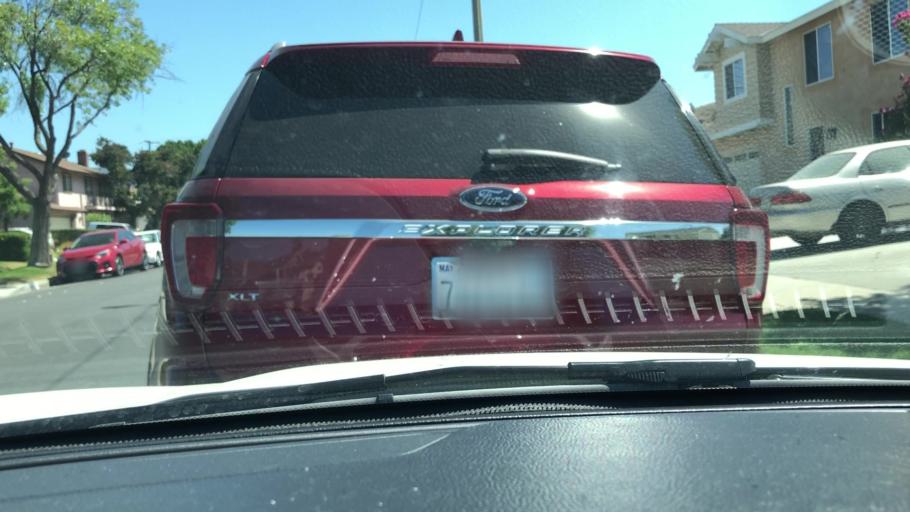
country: US
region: California
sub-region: Los Angeles County
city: Santa Clarita
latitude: 34.4222
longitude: -118.4846
